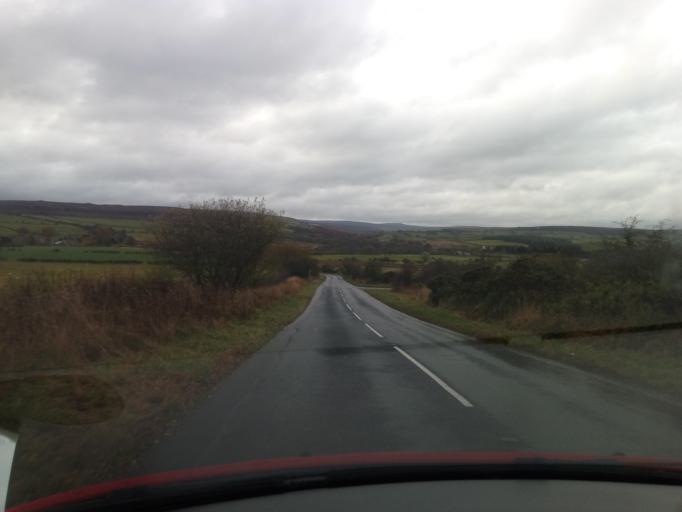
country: GB
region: England
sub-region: County Durham
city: Muggleswick
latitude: 54.8600
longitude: -1.9350
